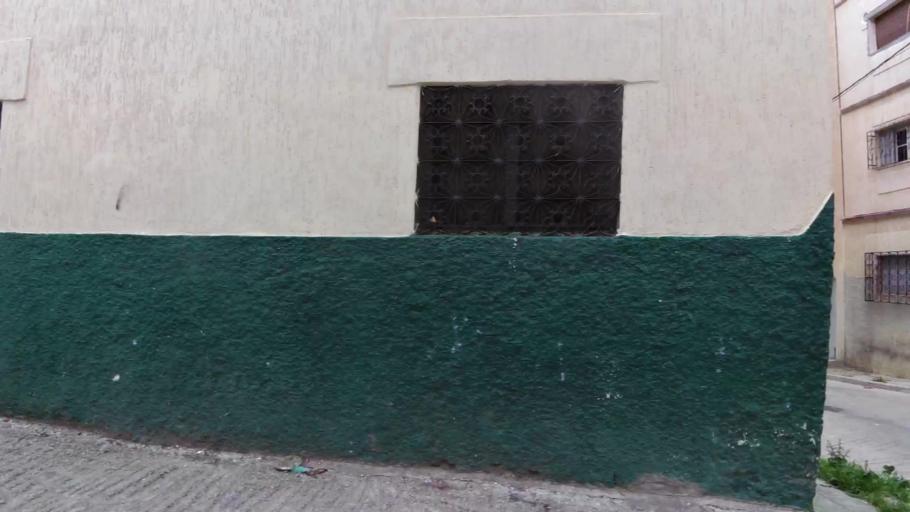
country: MA
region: Tanger-Tetouan
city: Tetouan
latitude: 35.5725
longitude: -5.3922
